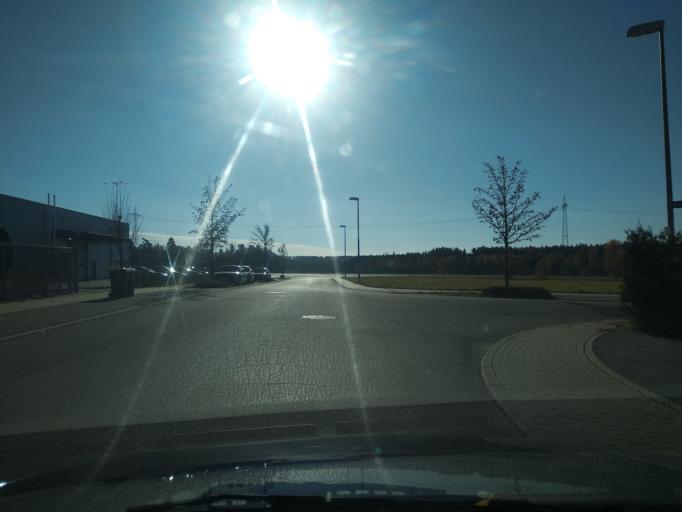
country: DE
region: Baden-Wuerttemberg
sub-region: Karlsruhe Region
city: Neuhausen
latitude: 48.7685
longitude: 8.7664
